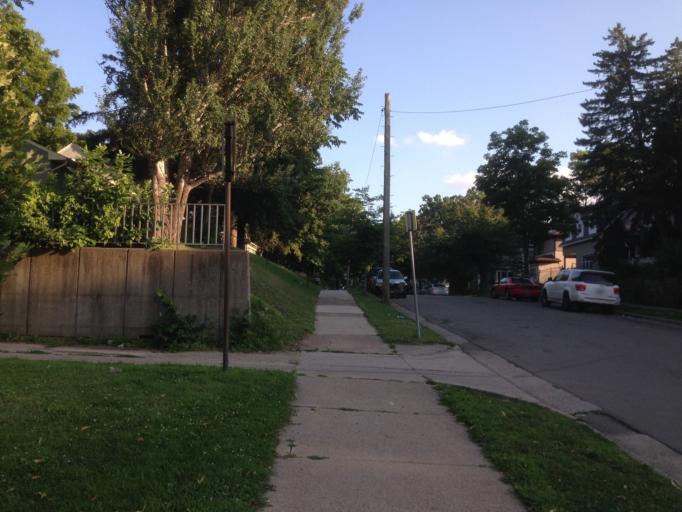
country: US
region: Minnesota
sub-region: Anoka County
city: Columbia Heights
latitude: 45.0125
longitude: -93.2968
